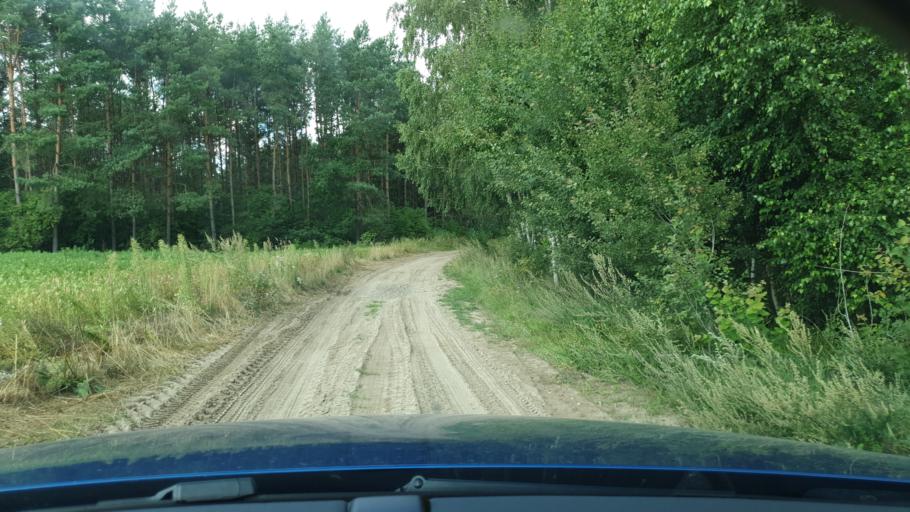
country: PL
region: Pomeranian Voivodeship
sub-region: Powiat czluchowski
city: Przechlewo
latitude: 53.8047
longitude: 17.3607
